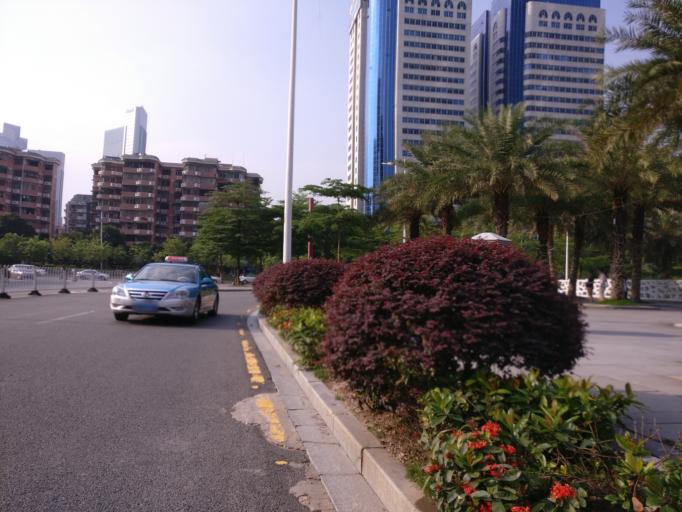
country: CN
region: Guangdong
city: Wushan
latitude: 23.1291
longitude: 113.3189
